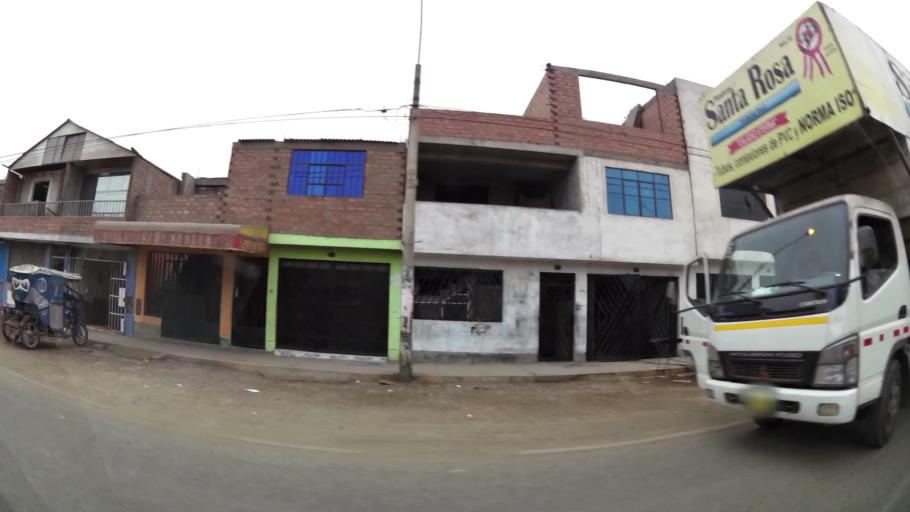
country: PE
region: Lima
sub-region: Lima
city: Urb. Santo Domingo
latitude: -11.9161
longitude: -77.0459
